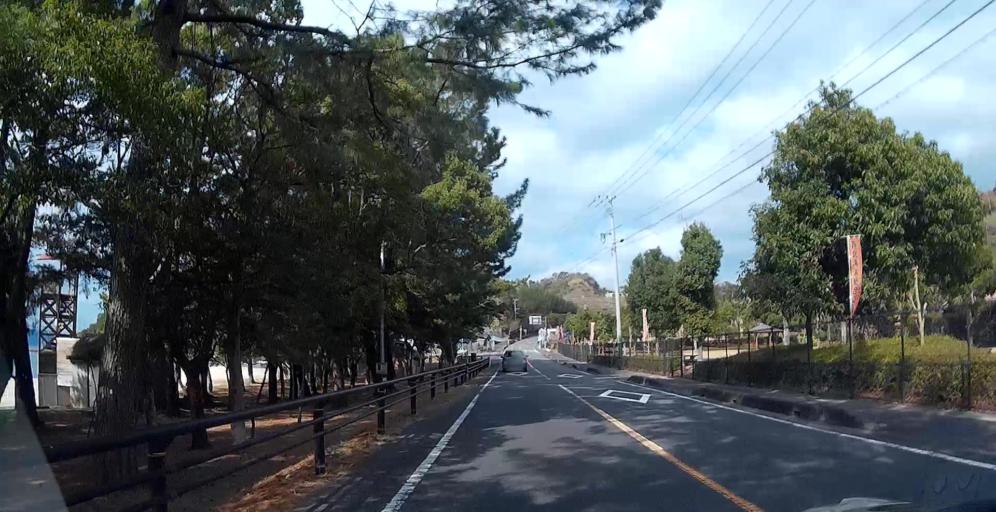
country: JP
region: Kumamoto
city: Minamata
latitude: 32.3182
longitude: 130.4713
